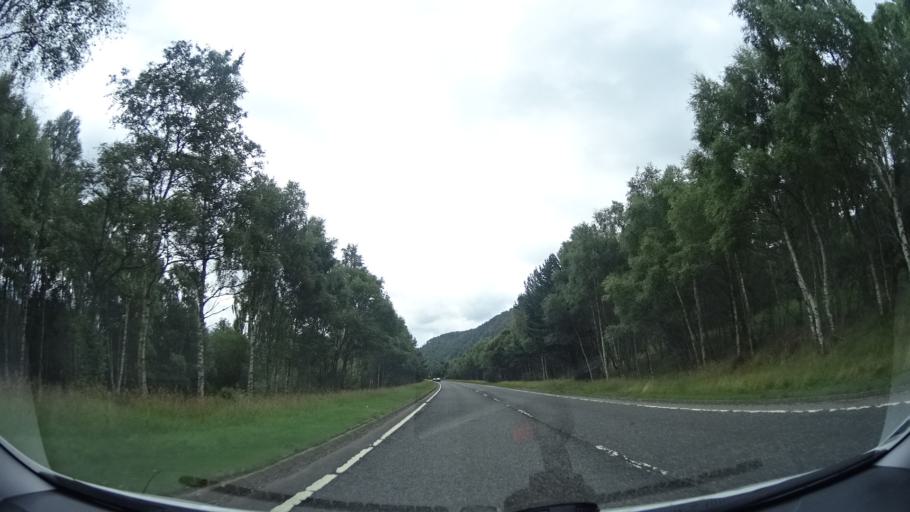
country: GB
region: Scotland
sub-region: Highland
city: Aviemore
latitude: 57.1932
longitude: -3.8368
